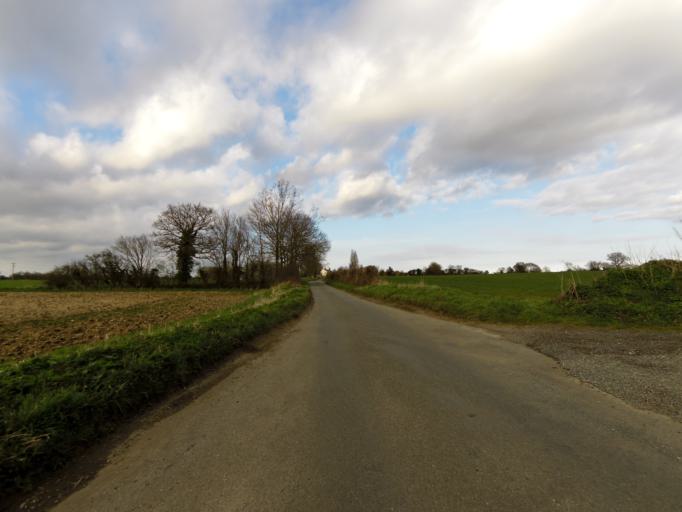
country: GB
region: England
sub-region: Suffolk
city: Ipswich
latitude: 52.0878
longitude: 1.1870
